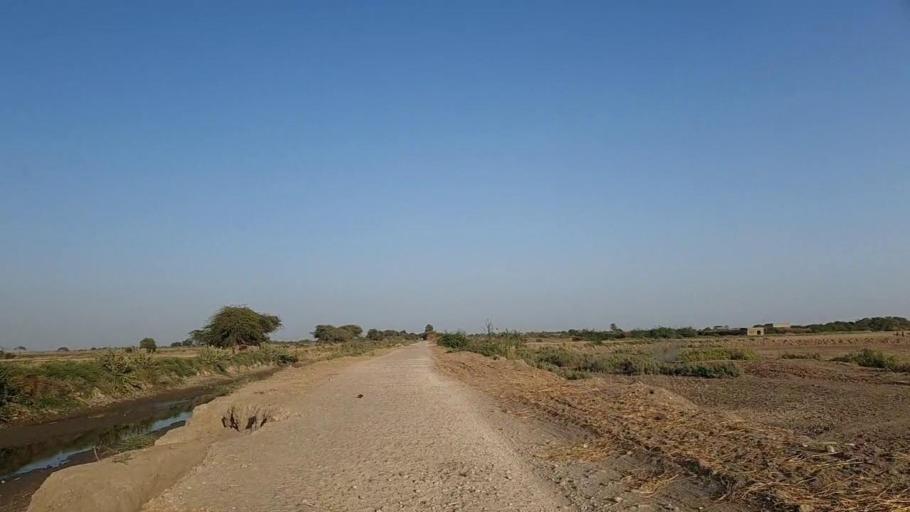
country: PK
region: Sindh
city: Jati
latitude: 24.4153
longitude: 68.3084
